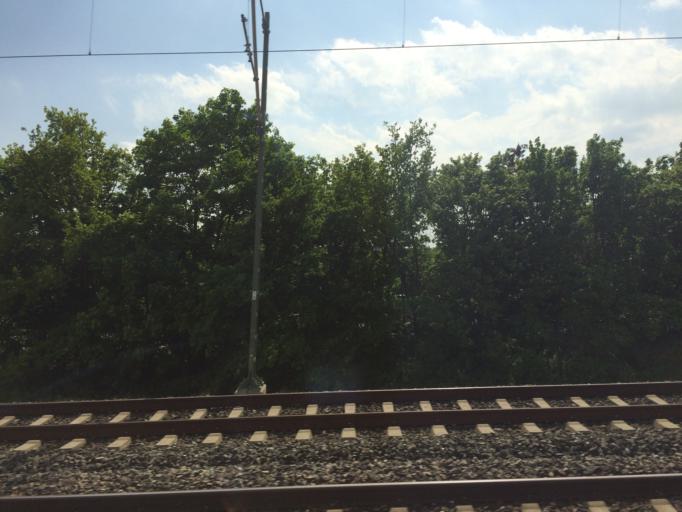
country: DE
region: Bavaria
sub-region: Regierungsbezirk Mittelfranken
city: Wetzendorf
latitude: 49.4479
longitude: 11.0490
